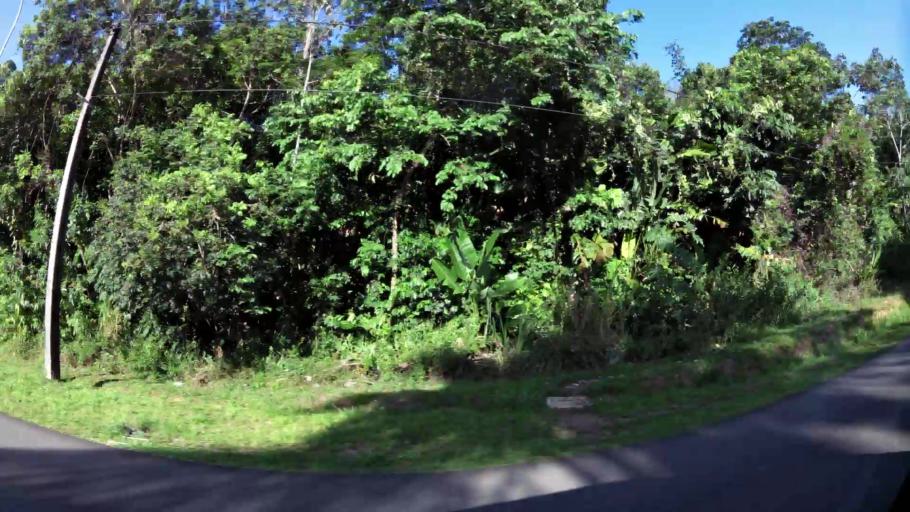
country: GF
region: Guyane
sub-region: Guyane
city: Remire-Montjoly
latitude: 4.8988
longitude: -52.2885
